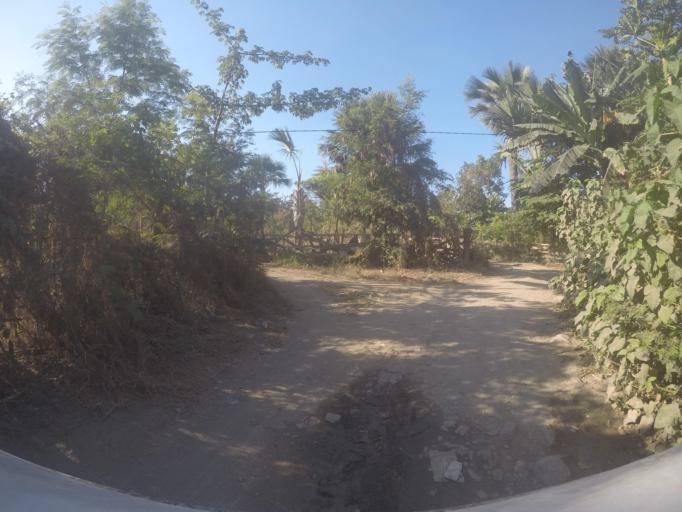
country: ID
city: Metinaro
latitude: -8.5463
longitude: 125.6667
